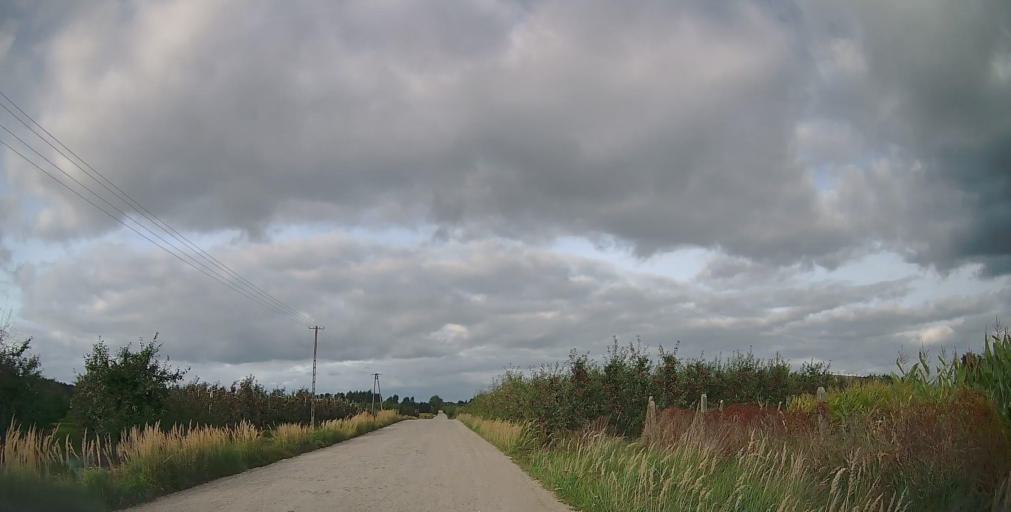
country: PL
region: Masovian Voivodeship
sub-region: Powiat grojecki
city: Jasieniec
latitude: 51.7730
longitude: 20.9211
